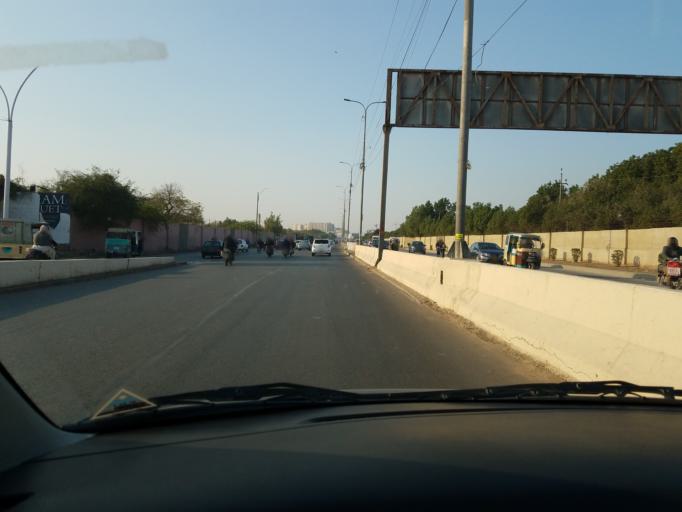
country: PK
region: Sindh
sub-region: Karachi District
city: Karachi
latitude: 24.8893
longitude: 67.1238
